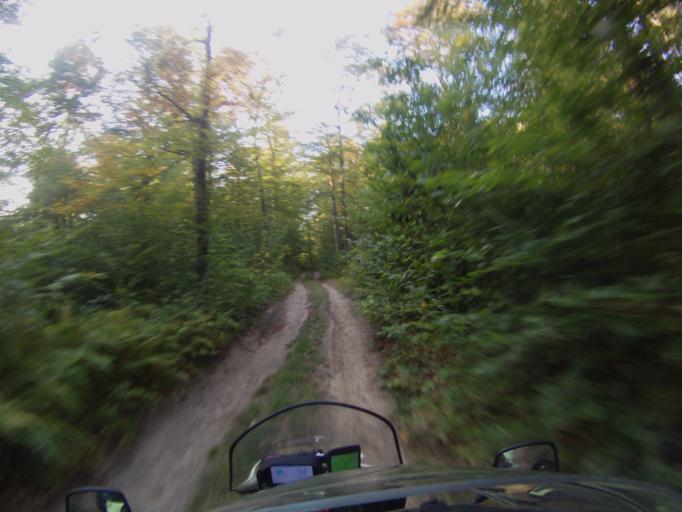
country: US
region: Vermont
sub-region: Addison County
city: Bristol
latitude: 44.0097
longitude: -73.0109
